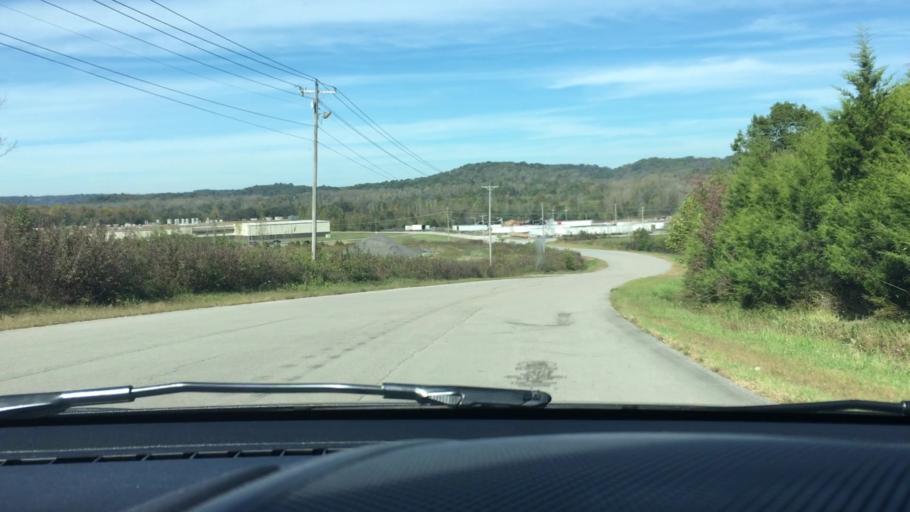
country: US
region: Tennessee
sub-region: Giles County
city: Pulaski
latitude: 35.2249
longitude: -87.0678
